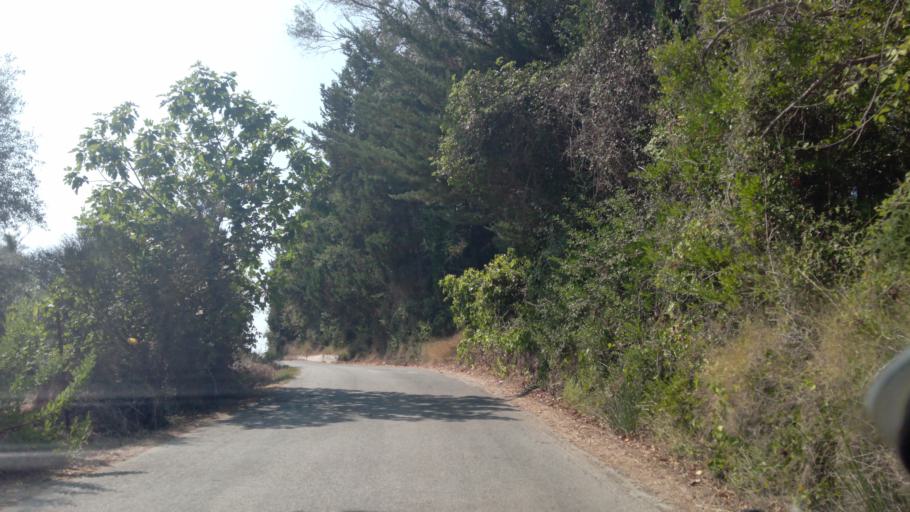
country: GR
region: Ionian Islands
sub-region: Nomos Kerkyras
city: Perivoli
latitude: 39.4007
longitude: 20.0247
